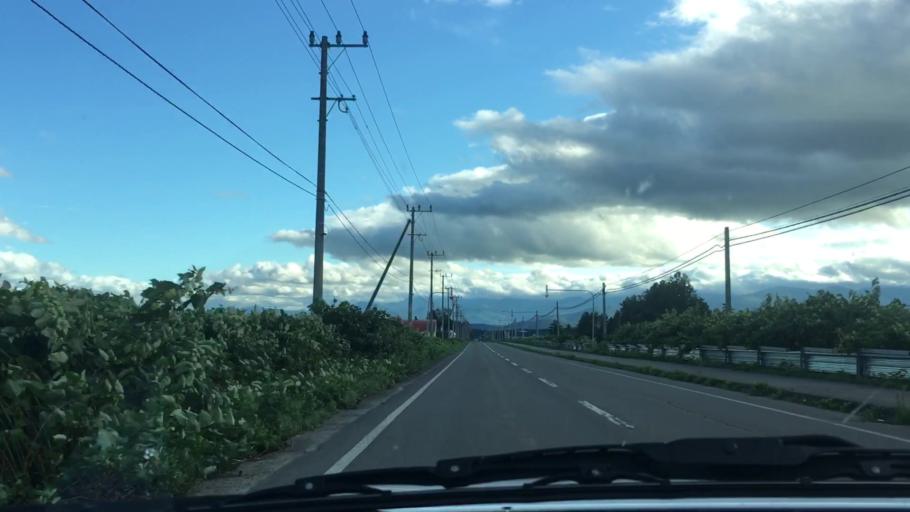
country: JP
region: Hokkaido
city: Otofuke
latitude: 43.1510
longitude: 142.9002
